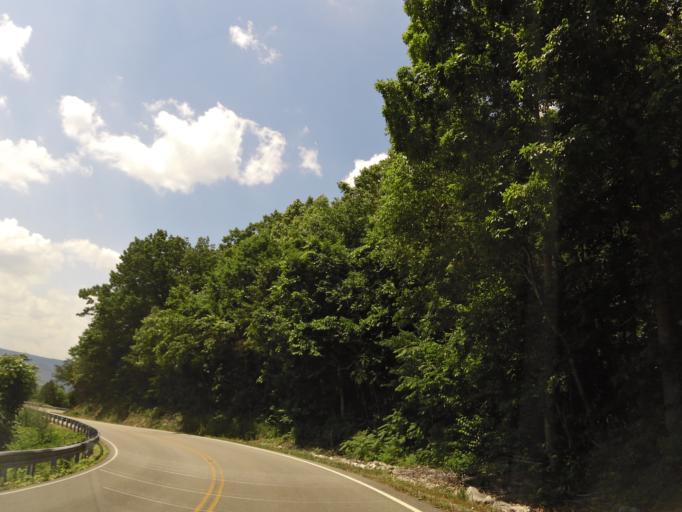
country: US
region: Tennessee
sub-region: Bledsoe County
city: Pikeville
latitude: 35.5725
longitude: -85.1535
